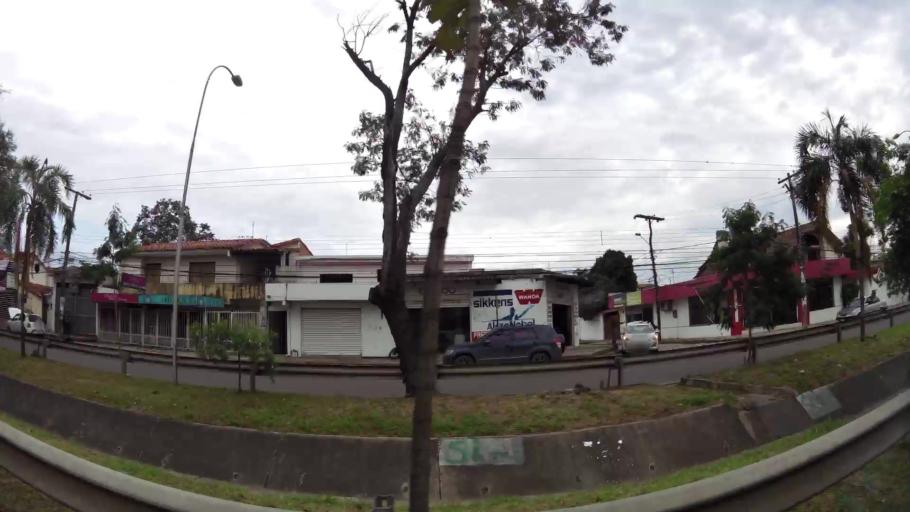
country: BO
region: Santa Cruz
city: Santa Cruz de la Sierra
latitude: -17.7706
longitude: -63.1669
